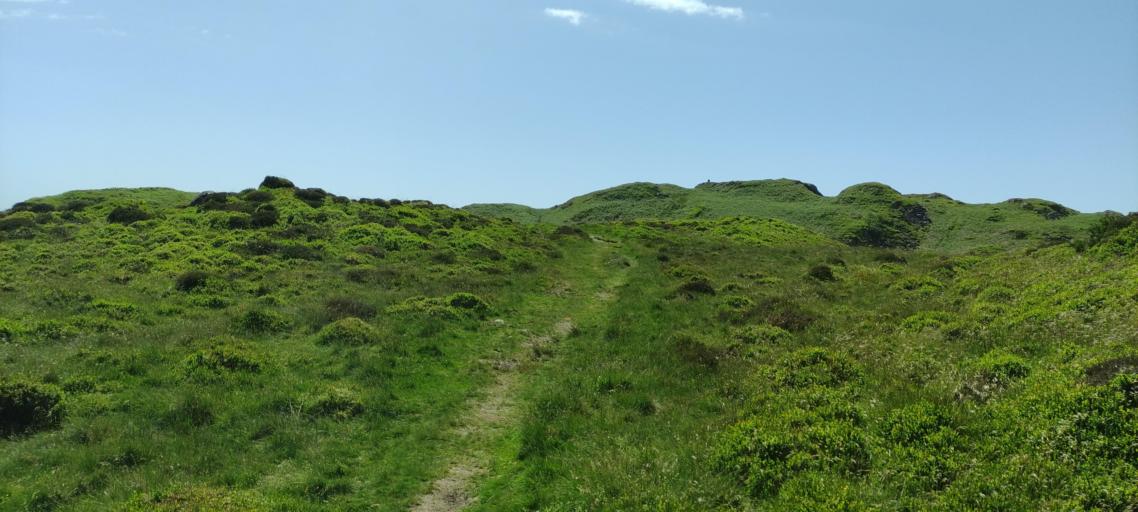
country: GB
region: England
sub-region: Cumbria
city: Seascale
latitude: 54.3744
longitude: -3.3646
